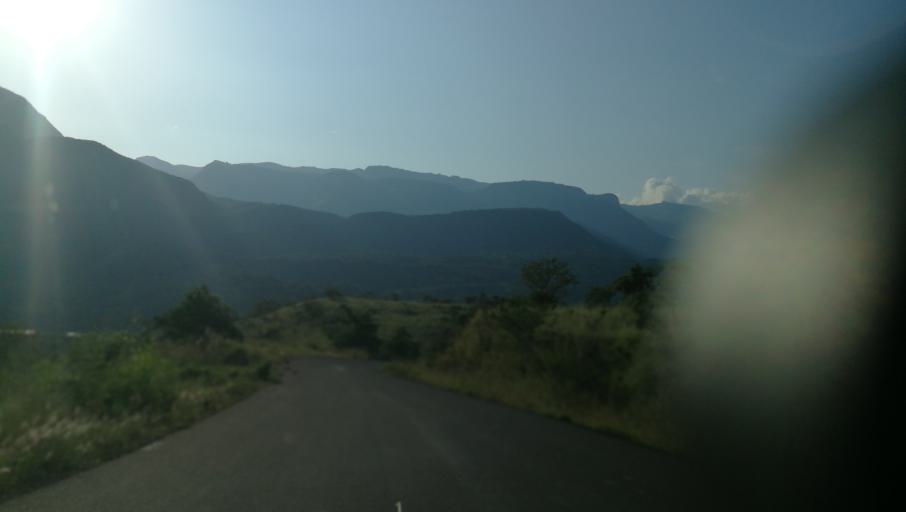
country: ET
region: Southern Nations, Nationalities, and People's Region
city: Areka
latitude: 6.8267
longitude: 37.2963
